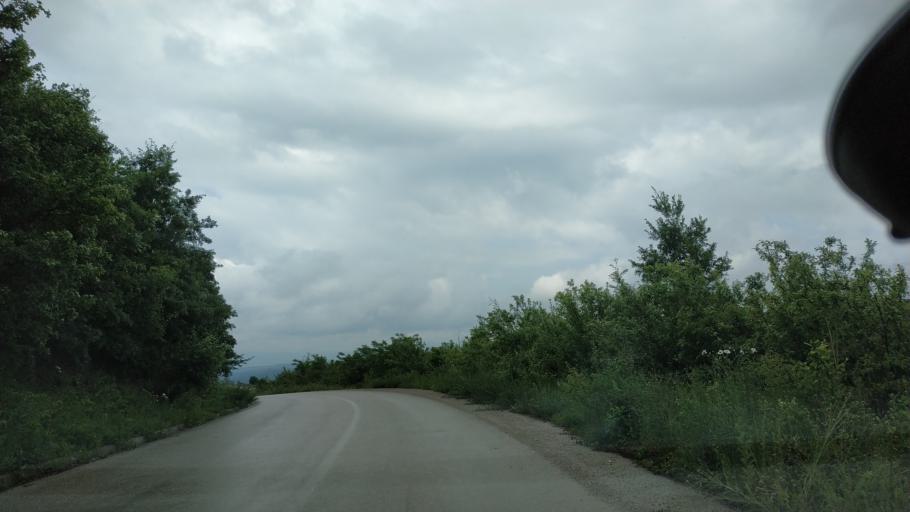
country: RS
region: Central Serbia
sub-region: Toplicki Okrug
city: Prokuplje
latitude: 43.4159
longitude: 21.5532
